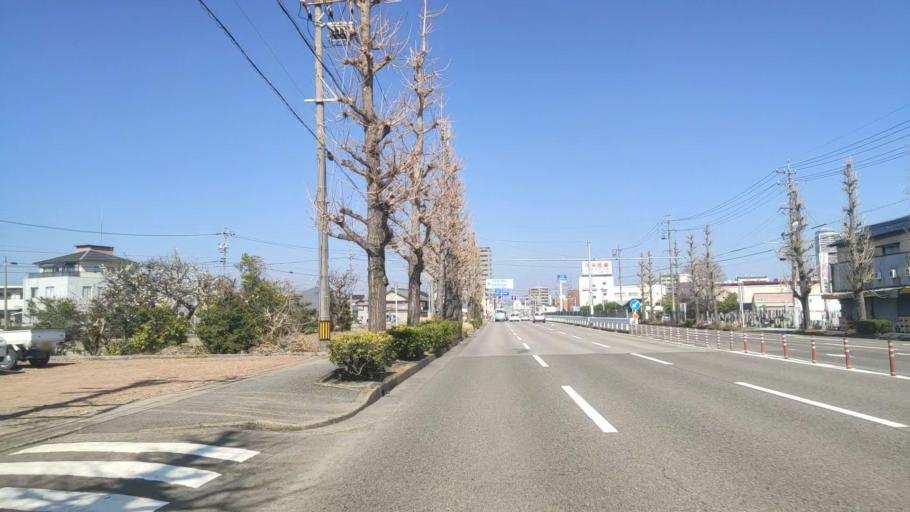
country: JP
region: Gifu
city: Gifu-shi
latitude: 35.3985
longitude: 136.7475
